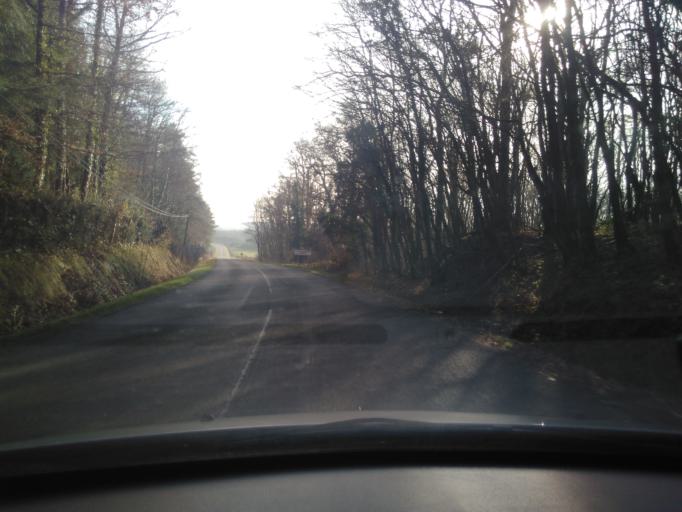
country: FR
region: Bourgogne
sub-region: Departement de la Nievre
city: Saint-Parize-le-Chatel
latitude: 46.8174
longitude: 3.2462
